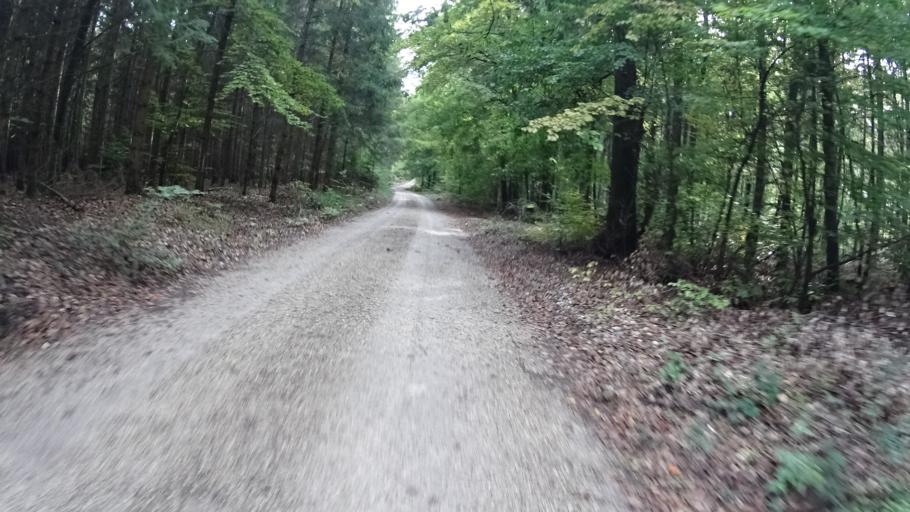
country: DE
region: Bavaria
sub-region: Upper Bavaria
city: Walting
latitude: 48.9113
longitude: 11.3249
